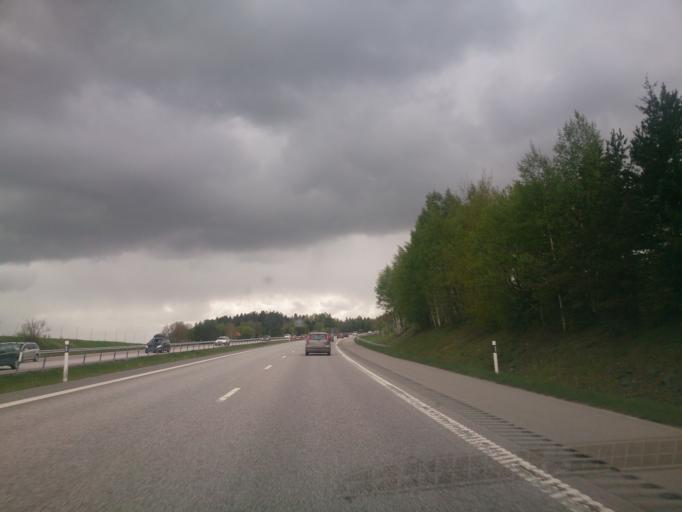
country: SE
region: Soedermanland
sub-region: Gnesta Kommun
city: Gnesta
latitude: 58.8788
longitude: 17.2400
